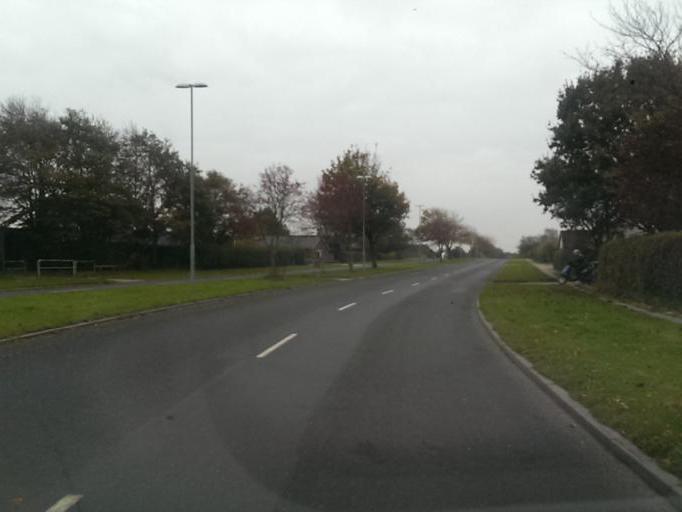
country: DK
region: South Denmark
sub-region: Esbjerg Kommune
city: Esbjerg
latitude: 55.5195
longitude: 8.4467
